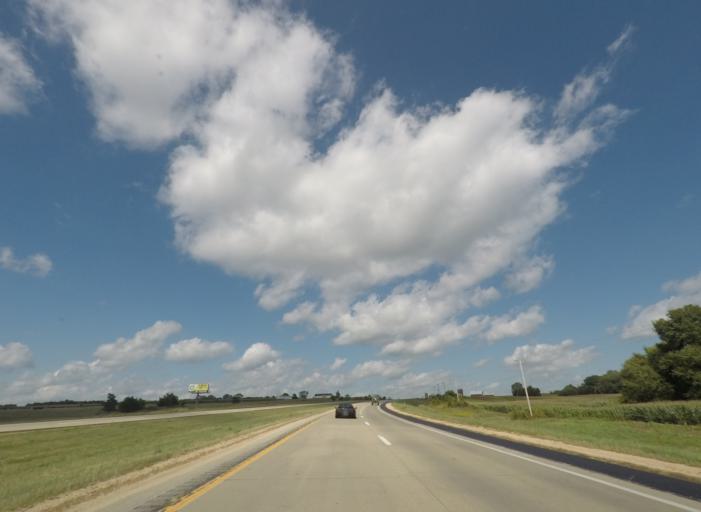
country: US
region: Iowa
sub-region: Jones County
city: Monticello
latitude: 42.2590
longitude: -91.1542
